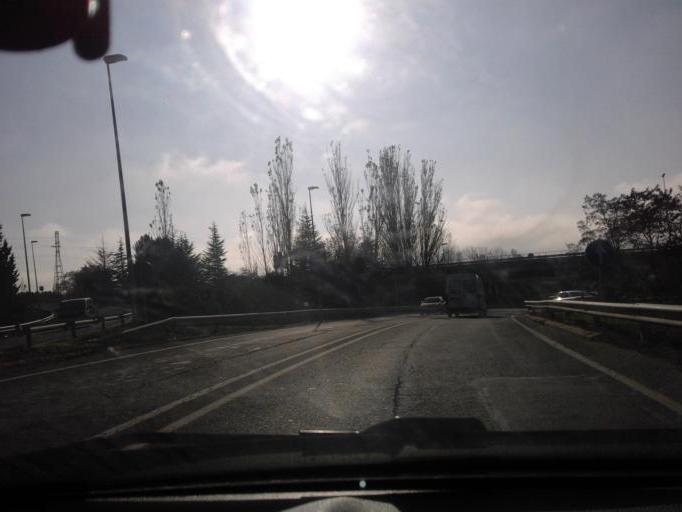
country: ES
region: Navarre
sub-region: Provincia de Navarra
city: Berriozar
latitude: 42.8412
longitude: -1.6817
